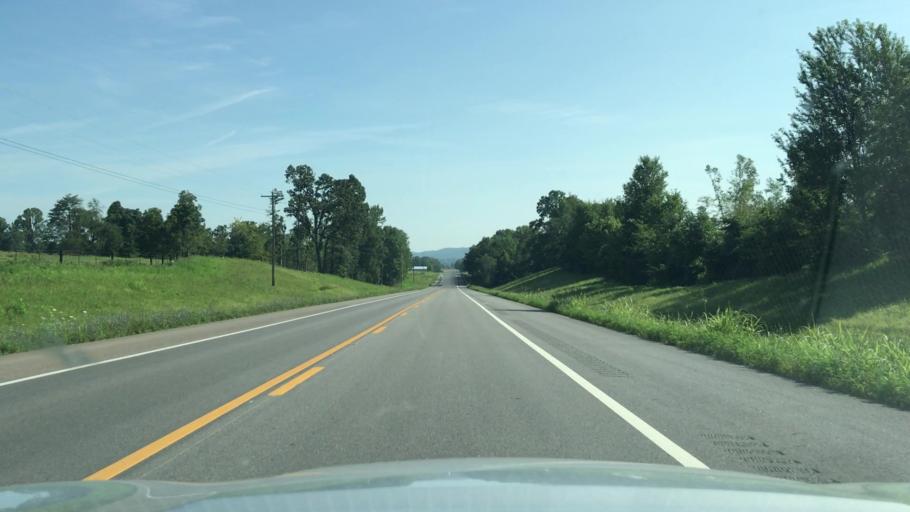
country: US
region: Tennessee
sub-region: Pickett County
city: Byrdstown
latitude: 36.5040
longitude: -85.1755
